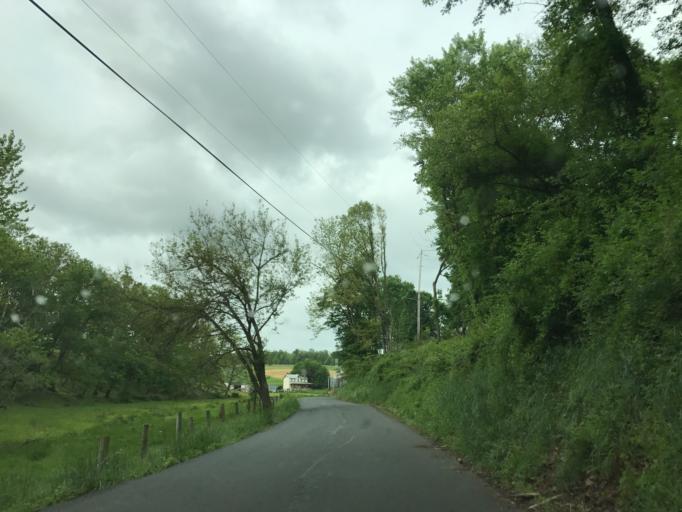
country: US
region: Maryland
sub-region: Carroll County
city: Hampstead
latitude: 39.5431
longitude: -76.9091
